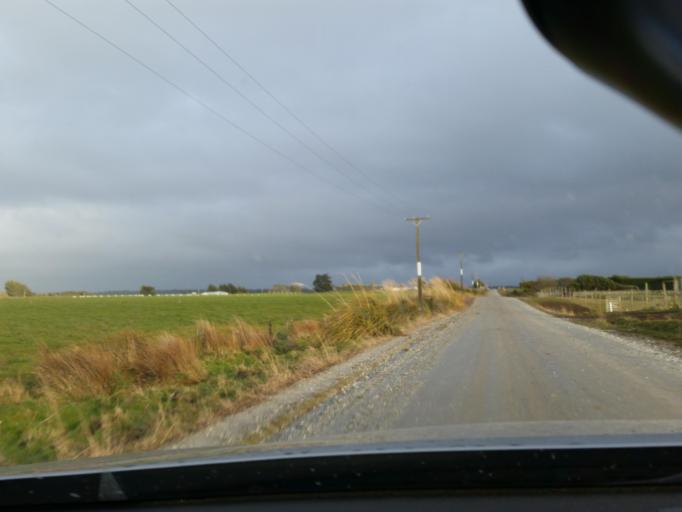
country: NZ
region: Southland
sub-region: Invercargill City
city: Invercargill
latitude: -46.4428
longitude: 168.5062
